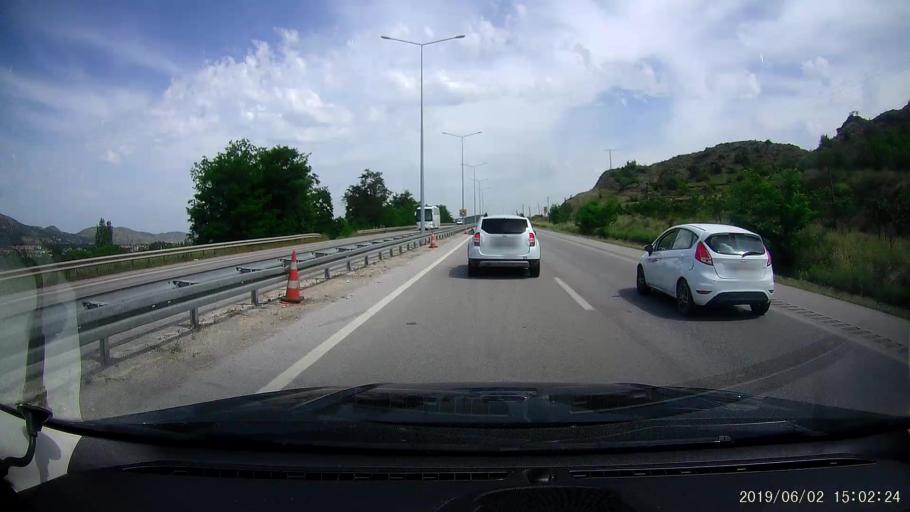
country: TR
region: Corum
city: Osmancik
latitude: 40.9813
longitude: 34.7665
